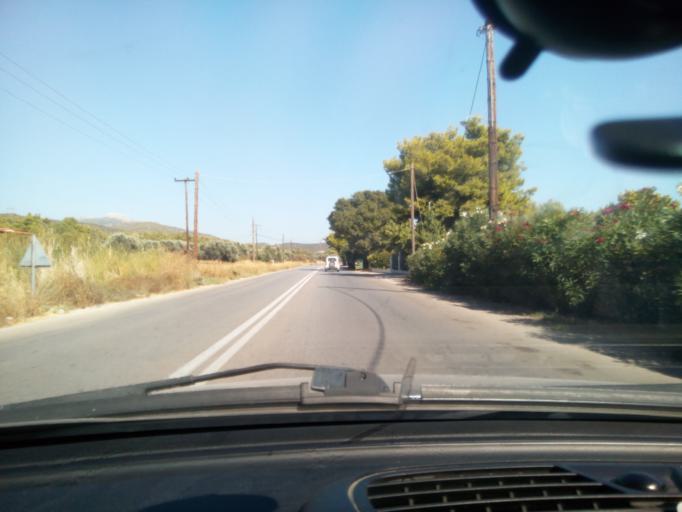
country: GR
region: Central Greece
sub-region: Nomos Evvoias
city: Filla
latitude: 38.4108
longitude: 23.7181
